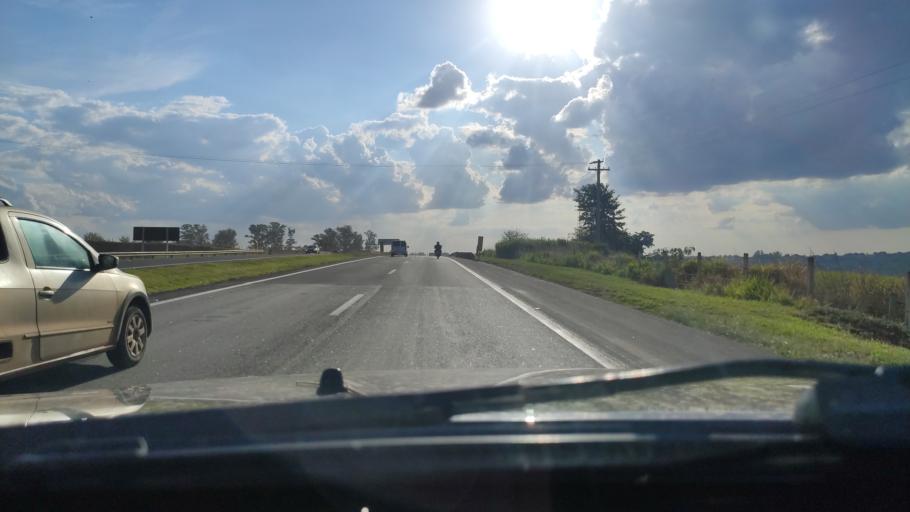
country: BR
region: Sao Paulo
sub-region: Mogi-Mirim
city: Mogi Mirim
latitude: -22.4558
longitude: -46.9150
